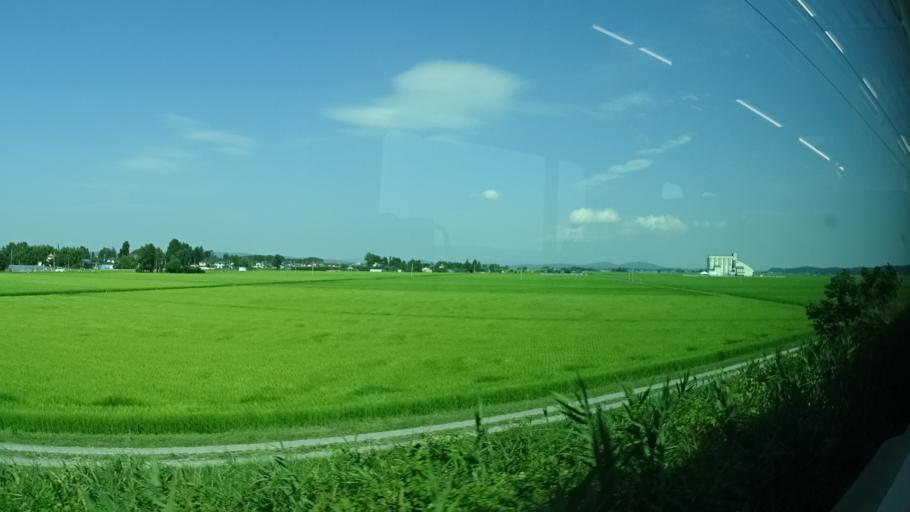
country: JP
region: Miyagi
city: Kogota
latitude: 38.5236
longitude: 141.0669
